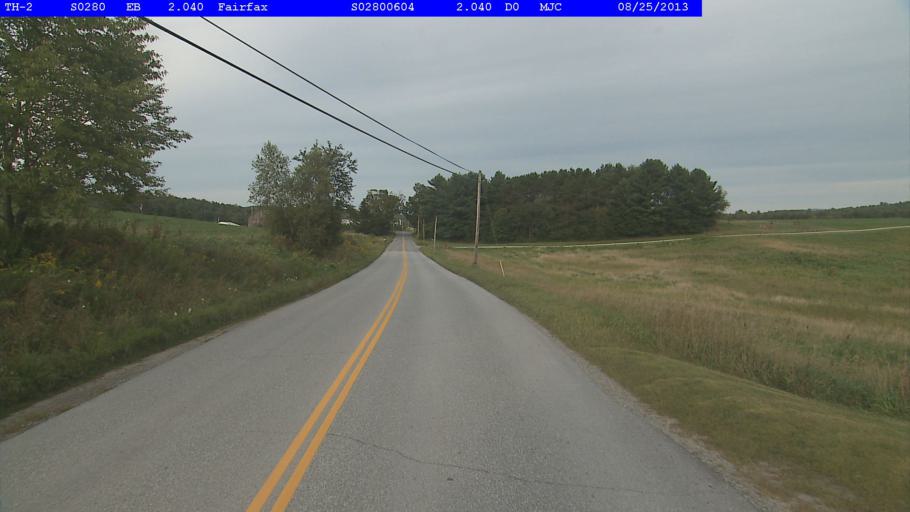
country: US
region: Vermont
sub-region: Chittenden County
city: Milton
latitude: 44.6710
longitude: -72.9712
